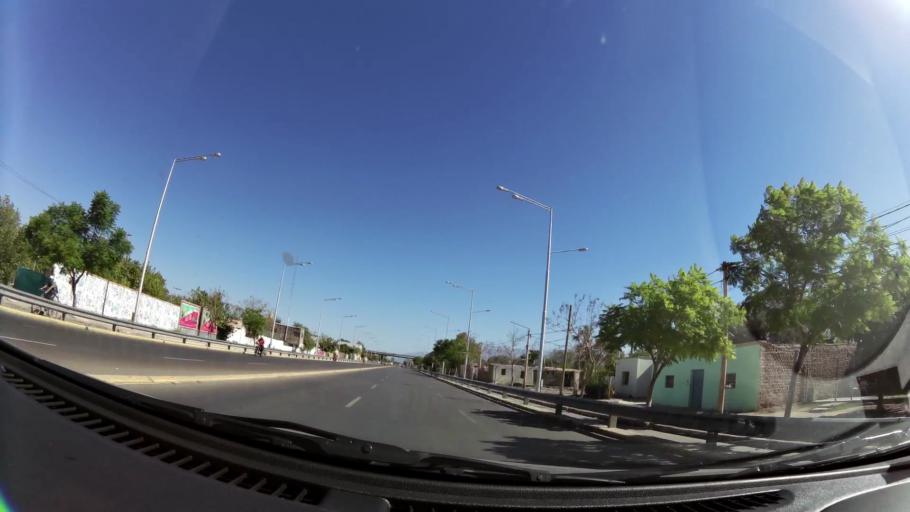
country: AR
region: San Juan
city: San Juan
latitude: -31.5511
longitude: -68.5381
